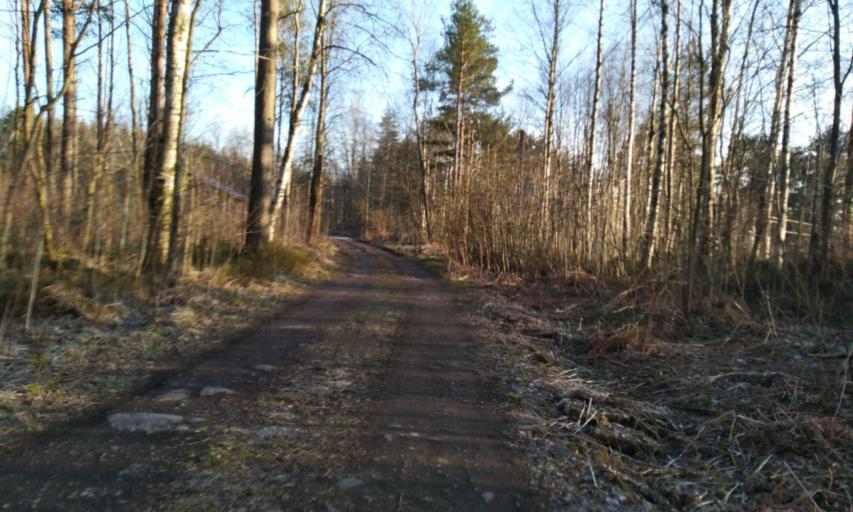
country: RU
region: Leningrad
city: Novoye Devyatkino
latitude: 60.1111
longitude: 30.4620
